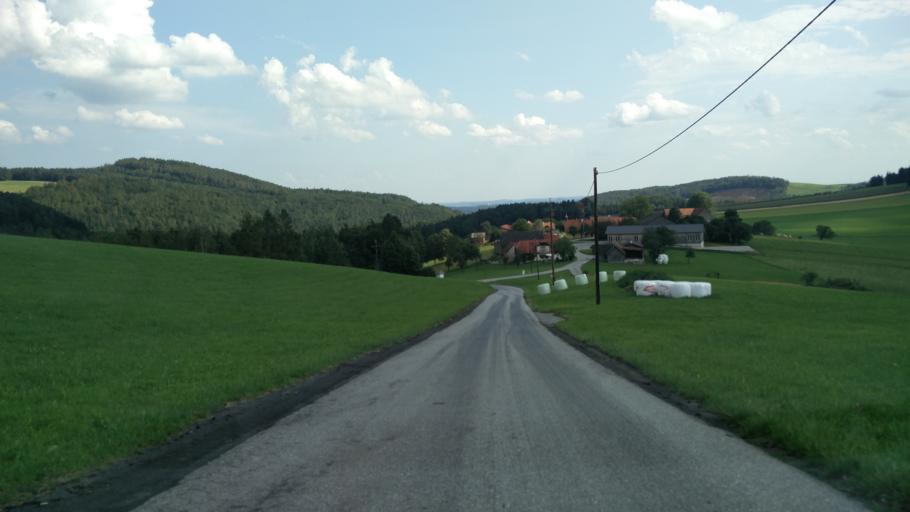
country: AT
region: Styria
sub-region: Politischer Bezirk Weiz
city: Naas
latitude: 47.2503
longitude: 15.6031
